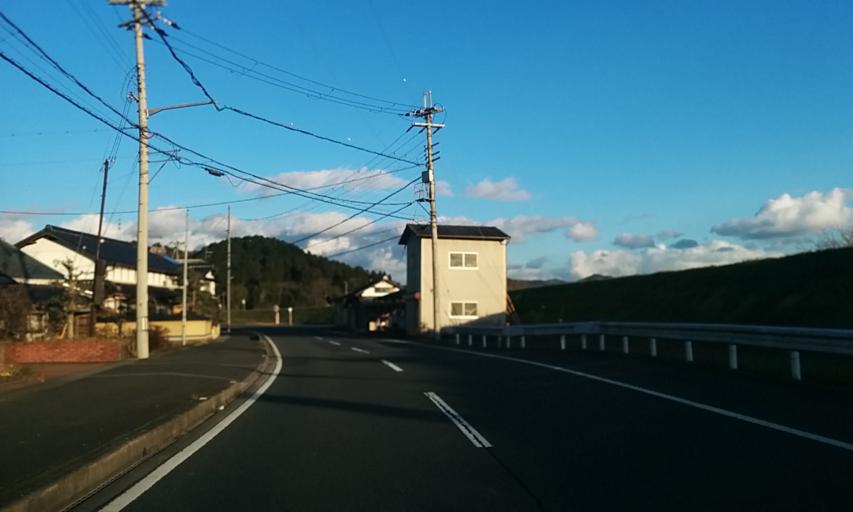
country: JP
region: Kyoto
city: Ayabe
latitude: 35.3132
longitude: 135.2493
